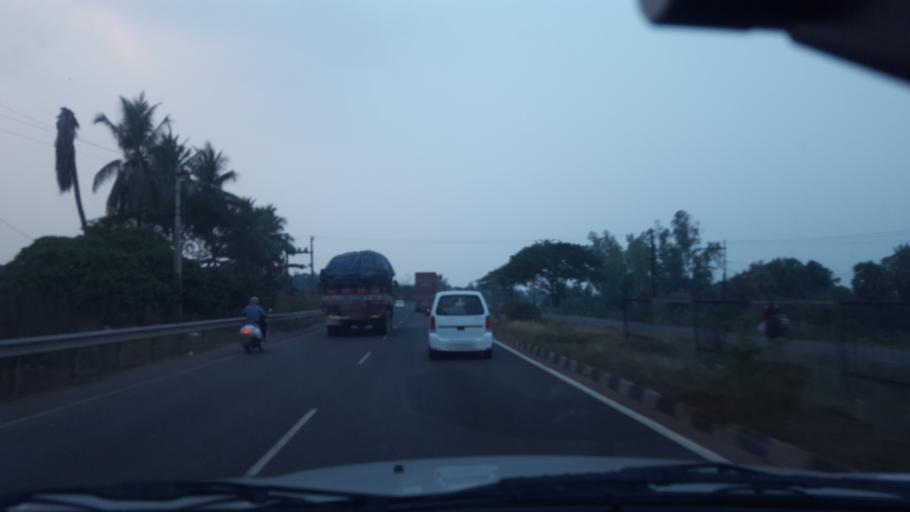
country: IN
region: Andhra Pradesh
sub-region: East Godavari
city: Rajahmundry
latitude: 16.9113
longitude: 81.7941
